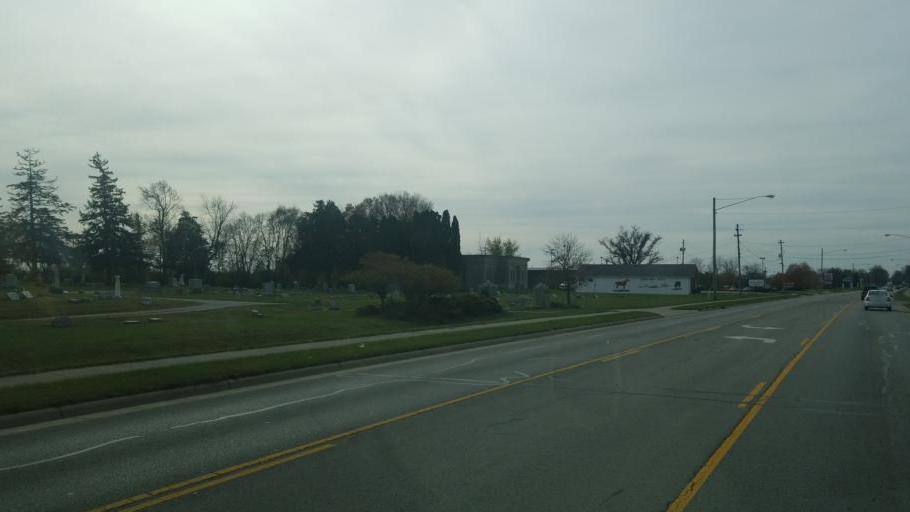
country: US
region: Ohio
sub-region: Madison County
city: London
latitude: 39.9010
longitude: -83.4332
